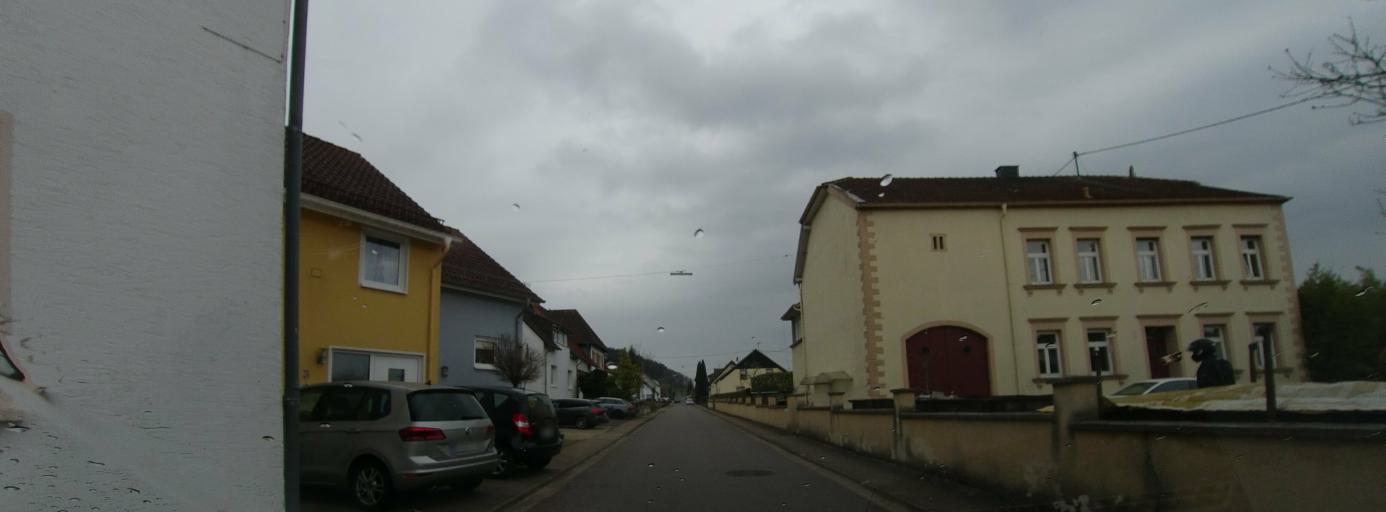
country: DE
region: Saarland
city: Losheim
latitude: 49.5062
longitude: 6.7439
